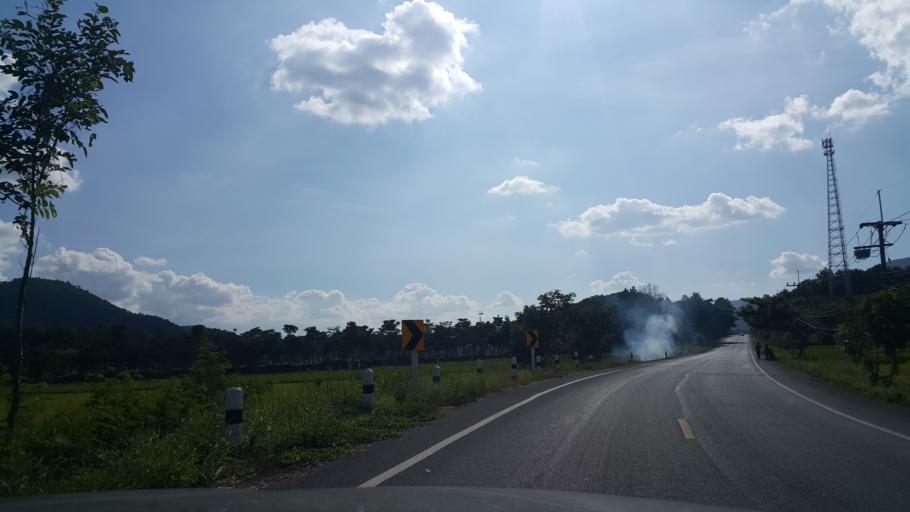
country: TH
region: Lamphun
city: Mae Tha
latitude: 18.5223
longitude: 99.2311
